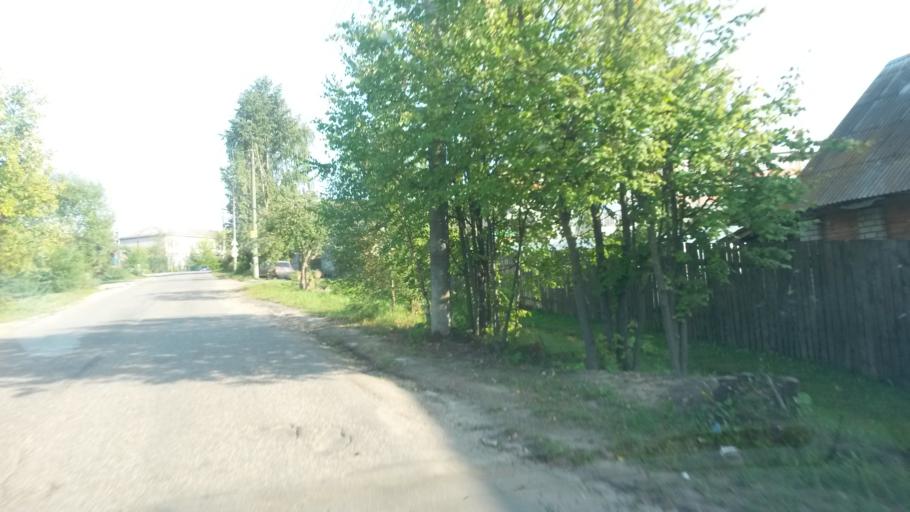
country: RU
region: Jaroslavl
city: Petrovsk
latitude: 57.0103
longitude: 39.2666
